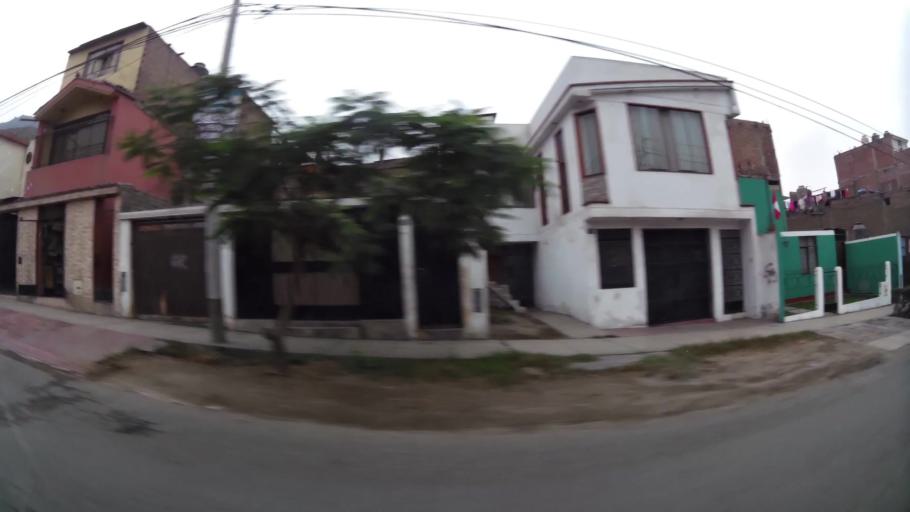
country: PE
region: Lima
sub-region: Lima
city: Vitarte
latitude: -12.0124
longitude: -76.9798
